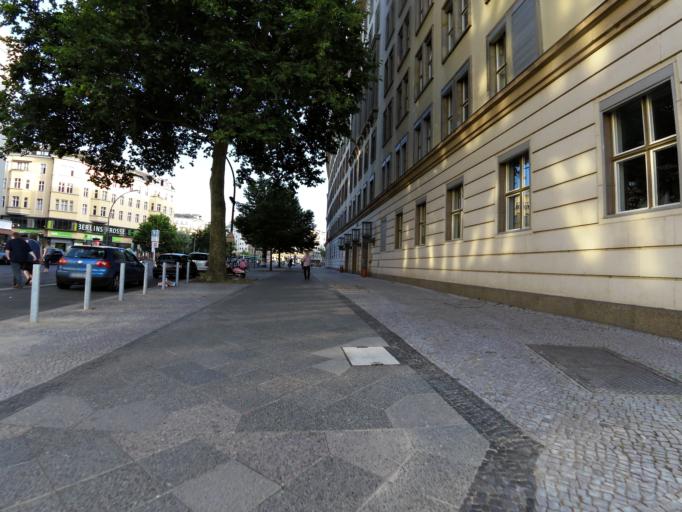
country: DE
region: Berlin
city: Berlin Schoeneberg
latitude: 52.4919
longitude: 13.3606
